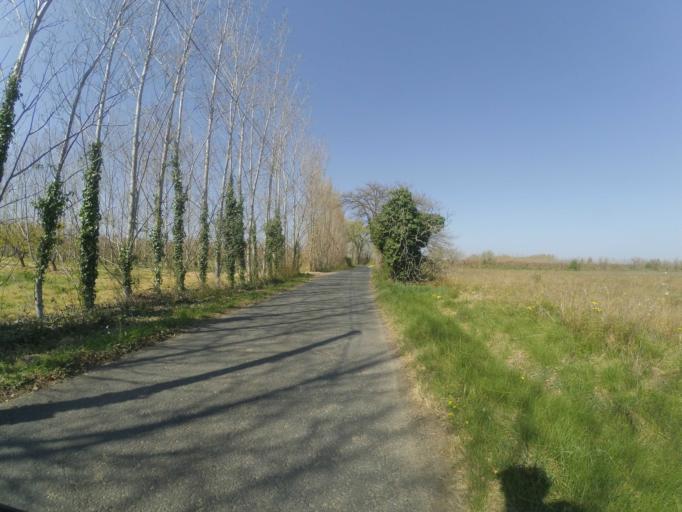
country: FR
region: Languedoc-Roussillon
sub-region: Departement des Pyrenees-Orientales
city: Thuir
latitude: 42.6538
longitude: 2.7627
